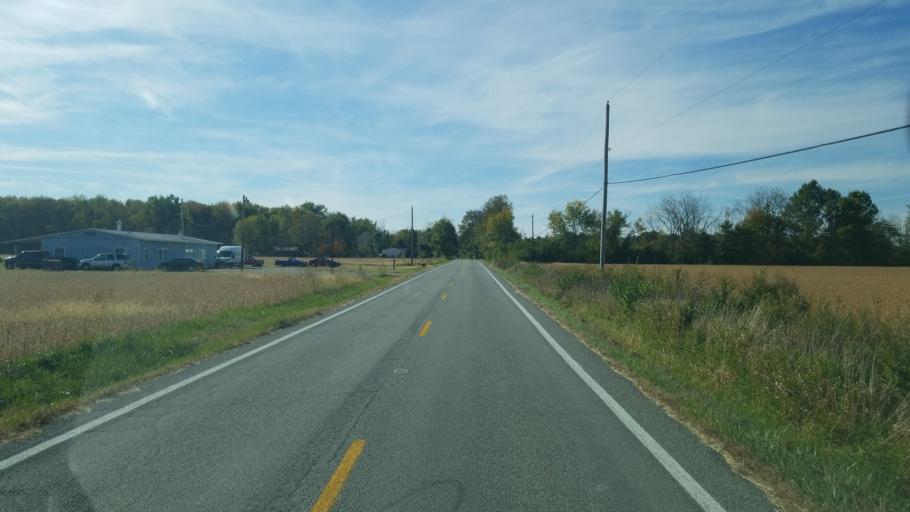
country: US
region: Ohio
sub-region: Clinton County
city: Blanchester
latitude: 39.4069
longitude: -84.0140
